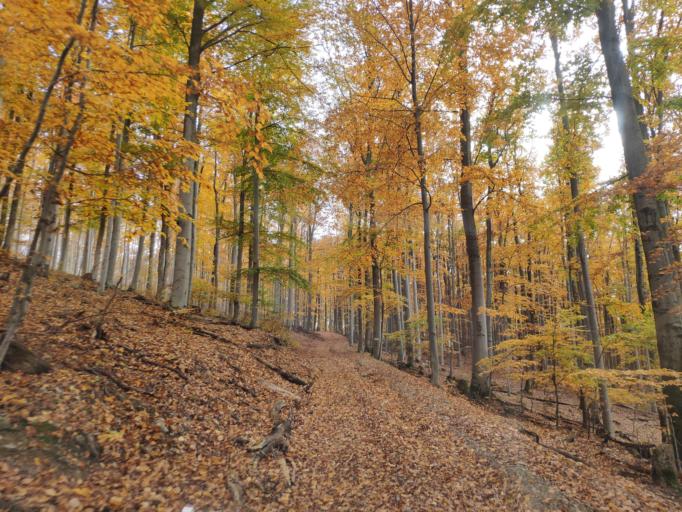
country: SK
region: Kosicky
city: Medzev
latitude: 48.7332
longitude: 20.9930
